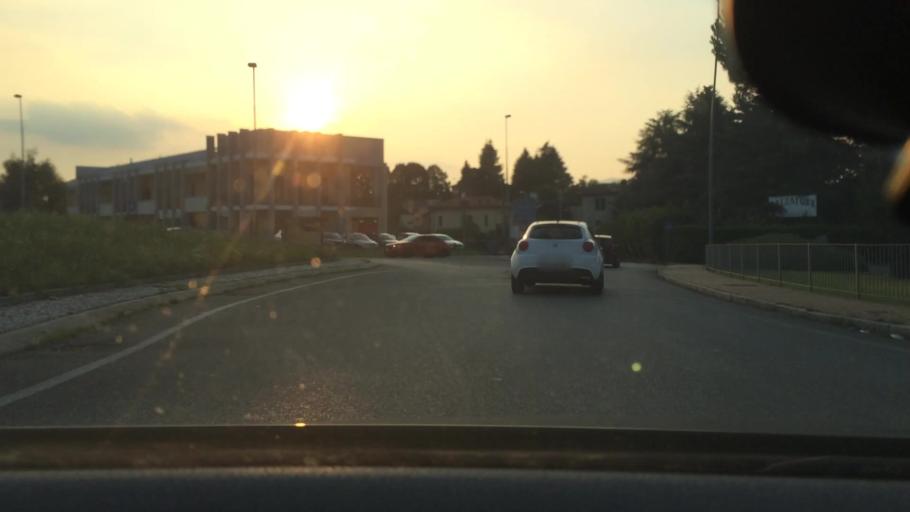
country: IT
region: Lombardy
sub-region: Provincia di Lecco
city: Sirtori
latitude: 45.7497
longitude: 9.3334
